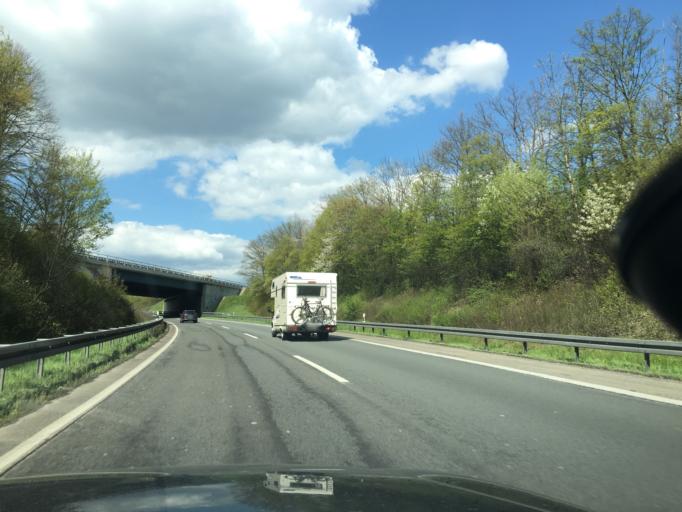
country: DE
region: Hesse
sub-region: Regierungsbezirk Darmstadt
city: Rockenberg
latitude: 50.4688
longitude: 8.7249
